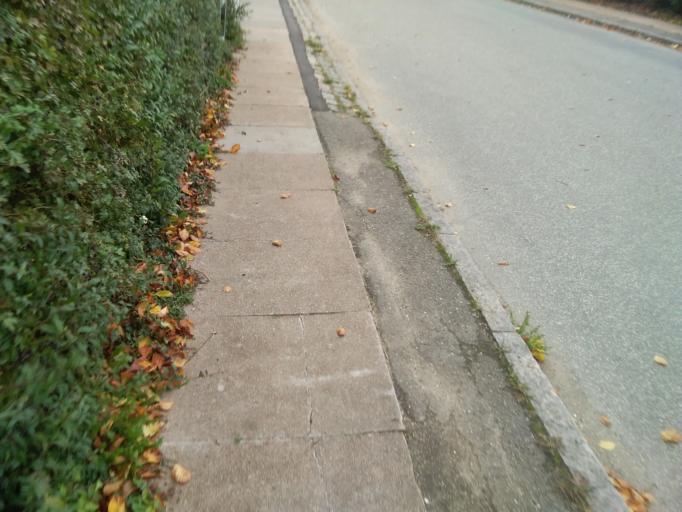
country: DK
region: Capital Region
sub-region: Rodovre Kommune
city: Rodovre
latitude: 55.7045
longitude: 12.4664
